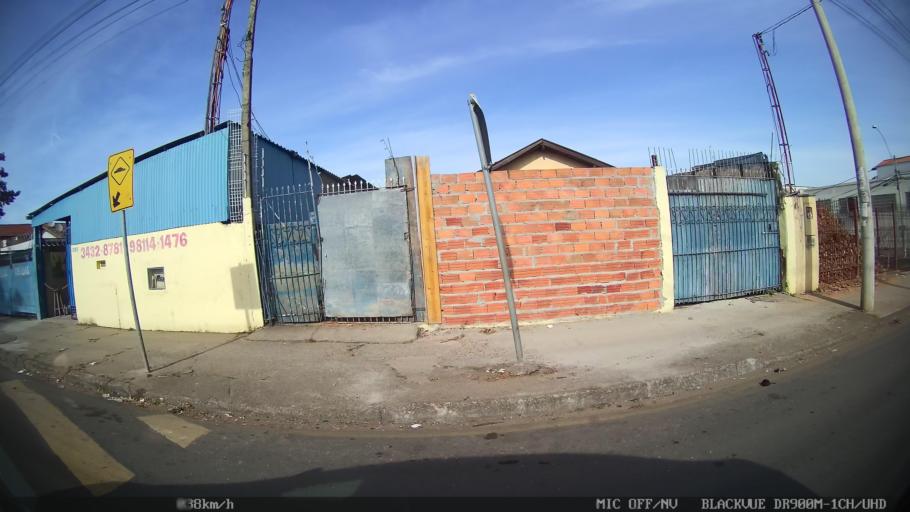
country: BR
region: Sao Paulo
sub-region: Piracicaba
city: Piracicaba
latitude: -22.7482
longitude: -47.6573
